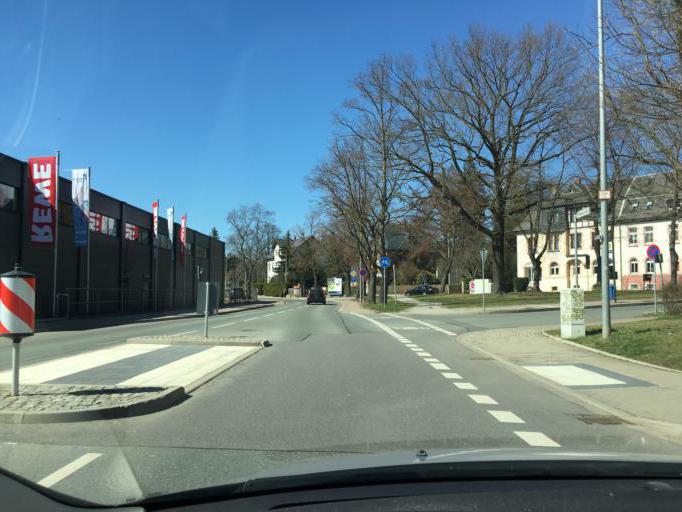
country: DE
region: Saxony
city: Neukirchen
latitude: 50.8263
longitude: 12.8317
